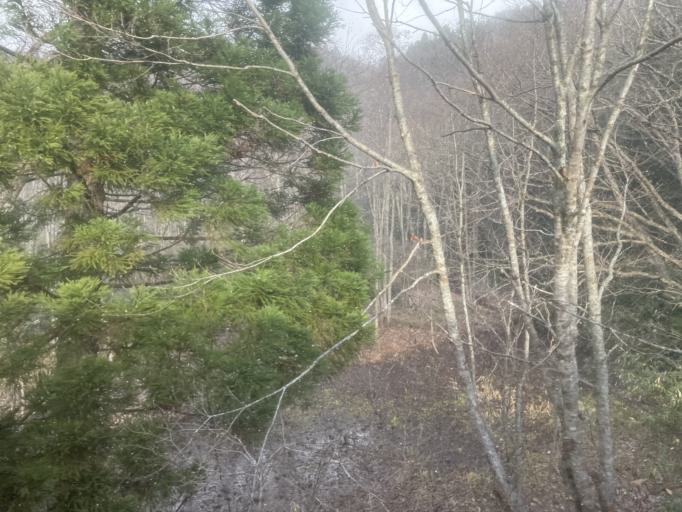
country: JP
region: Aomori
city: Goshogawara
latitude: 41.0810
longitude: 140.5244
